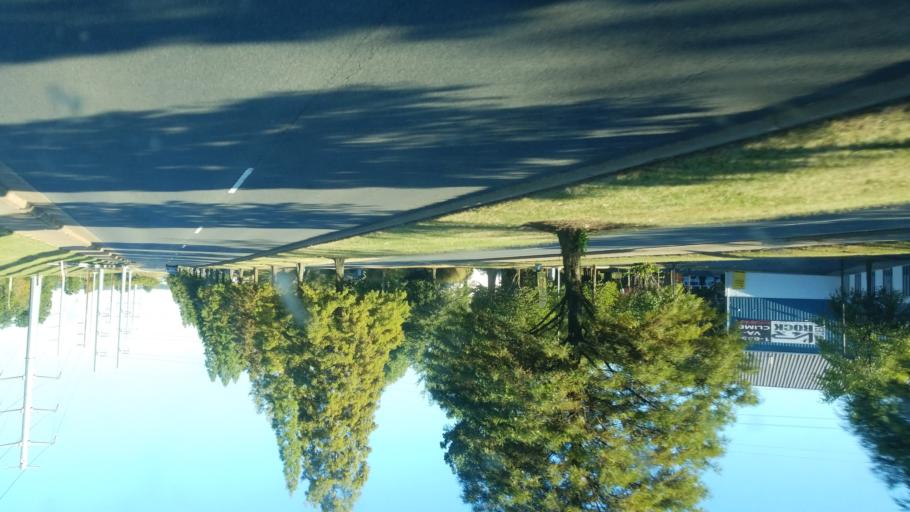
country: US
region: Virginia
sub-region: City of Manassas
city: Manassas
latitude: 38.7472
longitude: -77.5043
